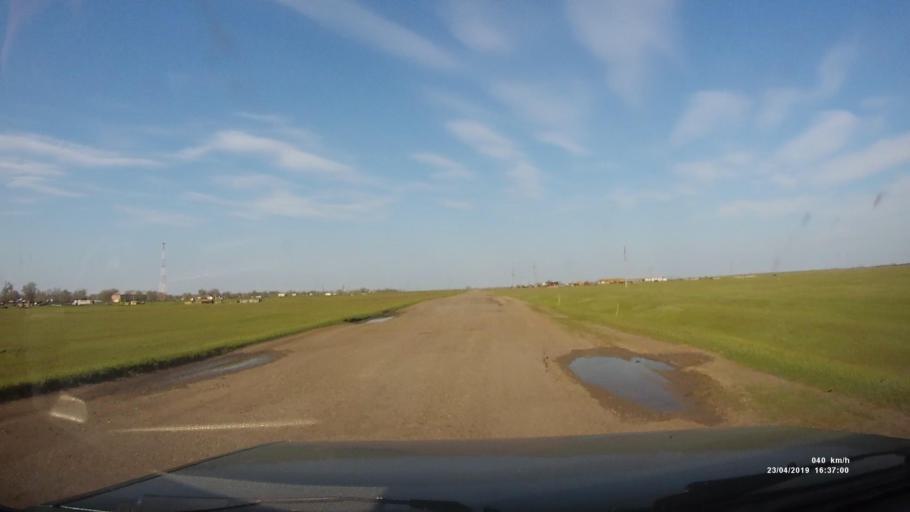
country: RU
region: Kalmykiya
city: Priyutnoye
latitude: 46.3316
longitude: 43.1434
